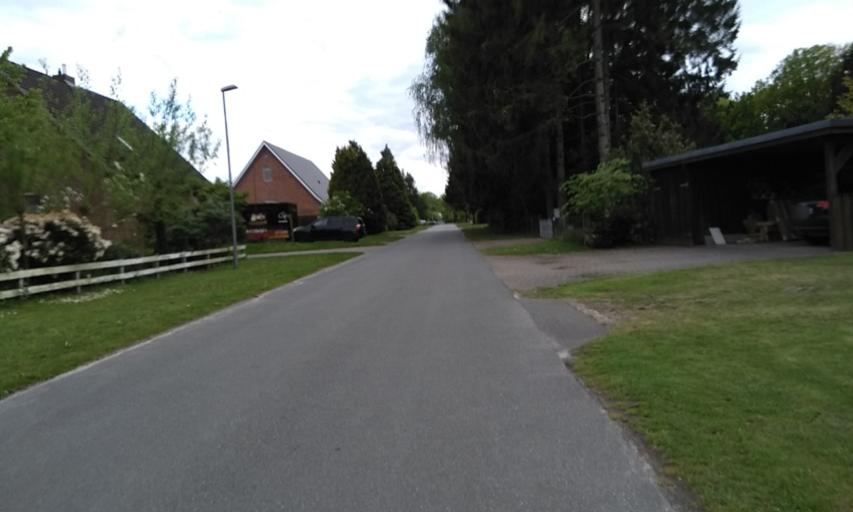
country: DE
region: Lower Saxony
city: Sauensiek
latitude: 53.3879
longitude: 9.5567
